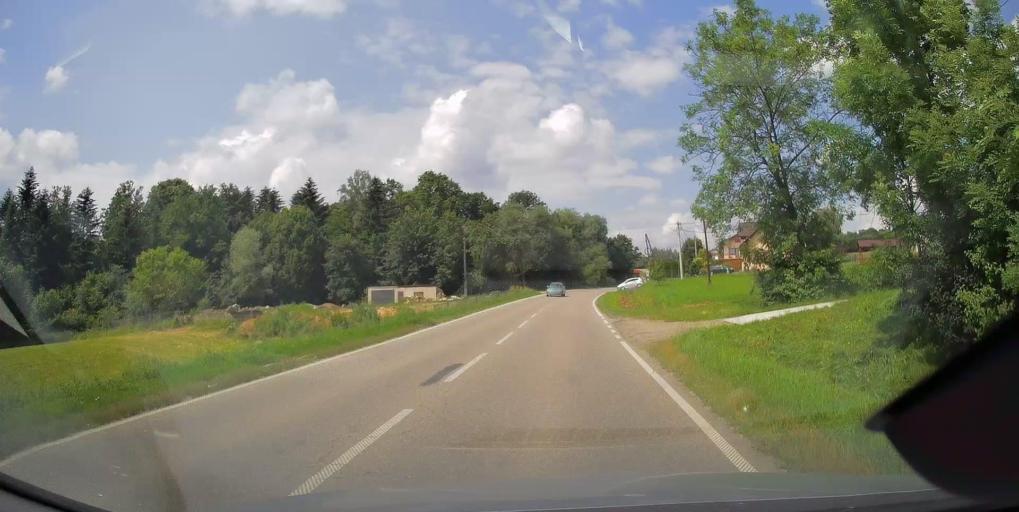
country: PL
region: Lesser Poland Voivodeship
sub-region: Powiat nowosadecki
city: Nowy Sacz
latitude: 49.6667
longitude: 20.7626
